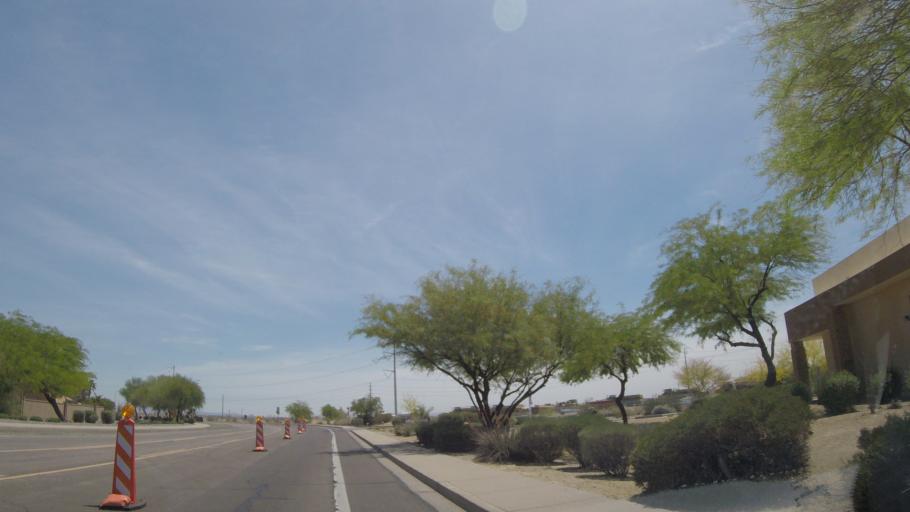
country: US
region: Arizona
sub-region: Maricopa County
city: Guadalupe
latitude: 33.2926
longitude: -112.0530
